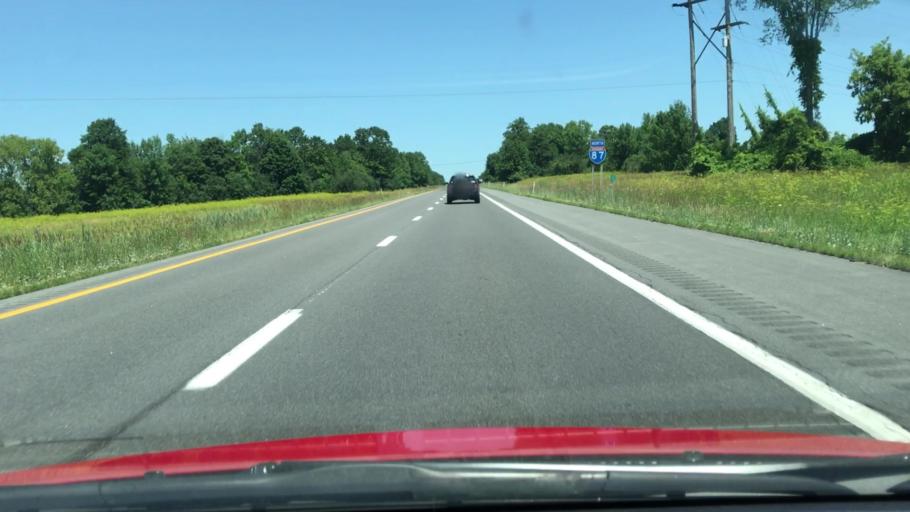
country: US
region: New York
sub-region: Clinton County
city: Cumberland Head
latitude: 44.7346
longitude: -73.4353
